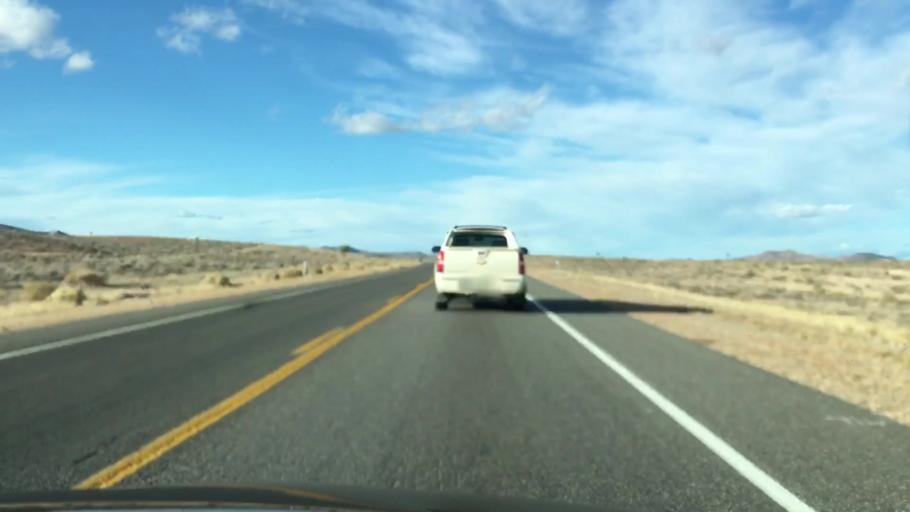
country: US
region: Nevada
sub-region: Esmeralda County
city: Goldfield
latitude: 37.5647
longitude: -117.1996
